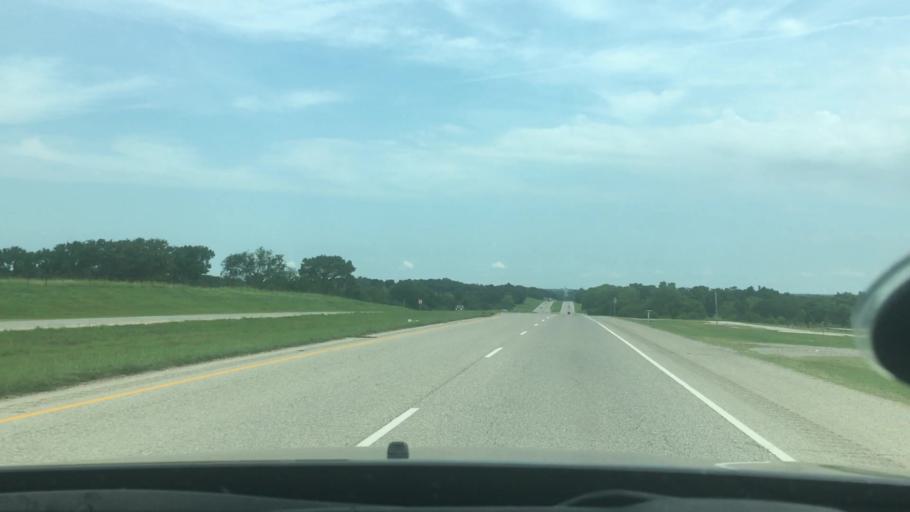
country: US
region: Oklahoma
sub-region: Seminole County
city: Seminole
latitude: 35.1966
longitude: -96.6749
